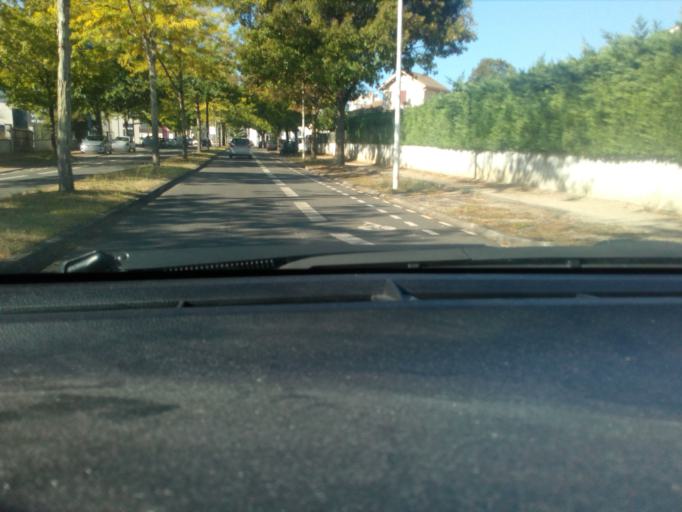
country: FR
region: Poitou-Charentes
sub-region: Departement de la Charente
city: Angouleme
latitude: 45.6503
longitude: 0.1356
